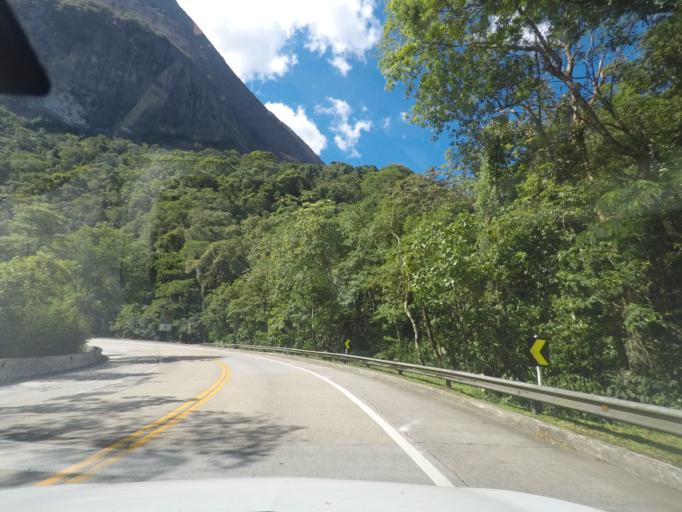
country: BR
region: Rio de Janeiro
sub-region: Guapimirim
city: Guapimirim
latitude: -22.4863
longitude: -42.9995
